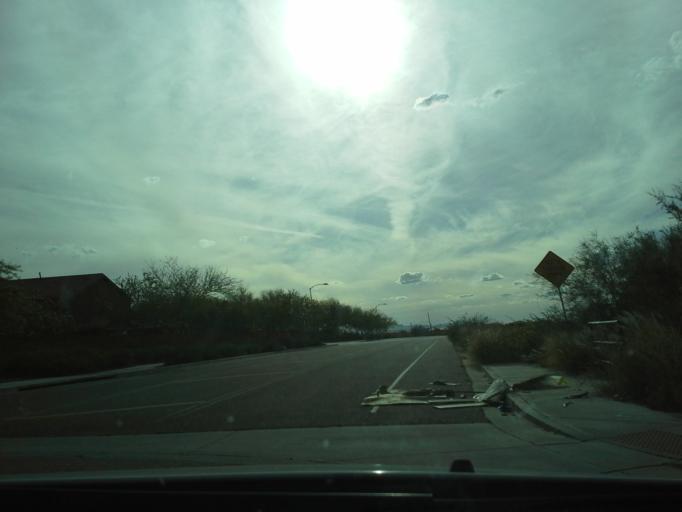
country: US
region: Arizona
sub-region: Maricopa County
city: Peoria
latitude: 33.6344
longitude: -112.2157
